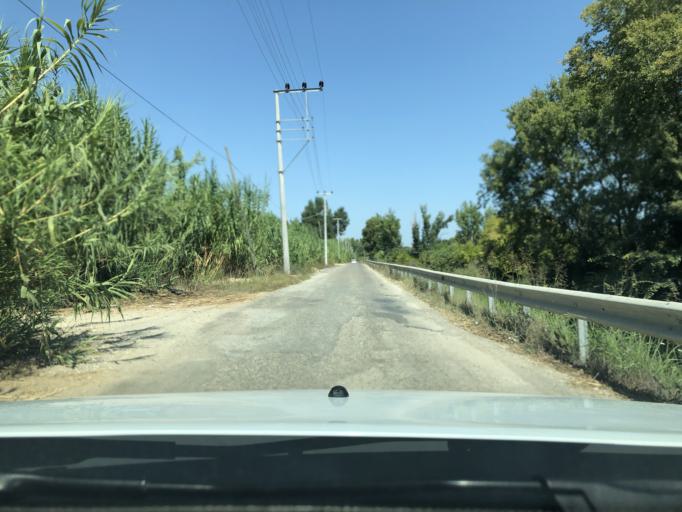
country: TR
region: Antalya
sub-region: Manavgat
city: Manavgat
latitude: 36.8037
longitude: 31.4678
